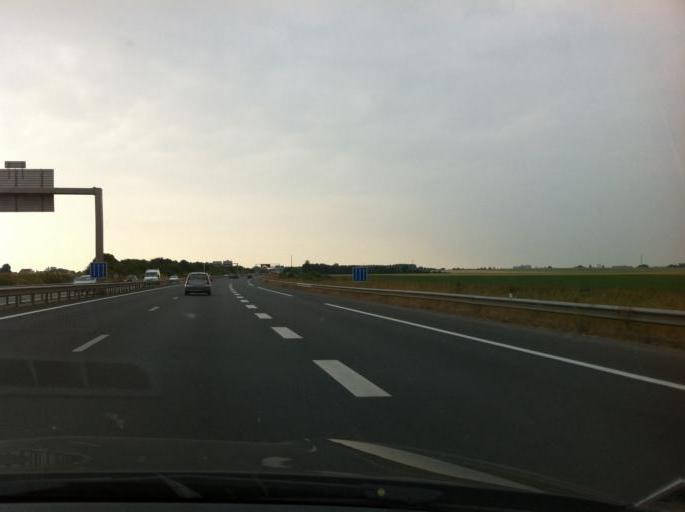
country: FR
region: Ile-de-France
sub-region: Departement de Seine-et-Marne
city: Vert-Saint-Denis
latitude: 48.5751
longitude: 2.6392
